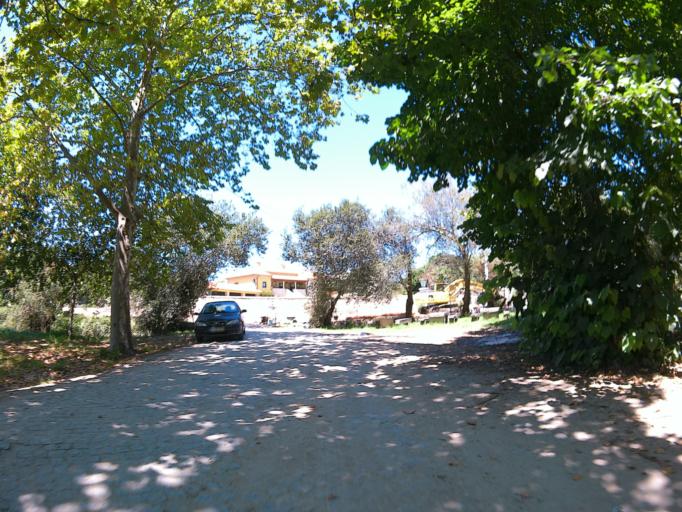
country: PT
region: Viana do Castelo
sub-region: Viana do Castelo
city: Darque
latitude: 41.7037
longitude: -8.7396
